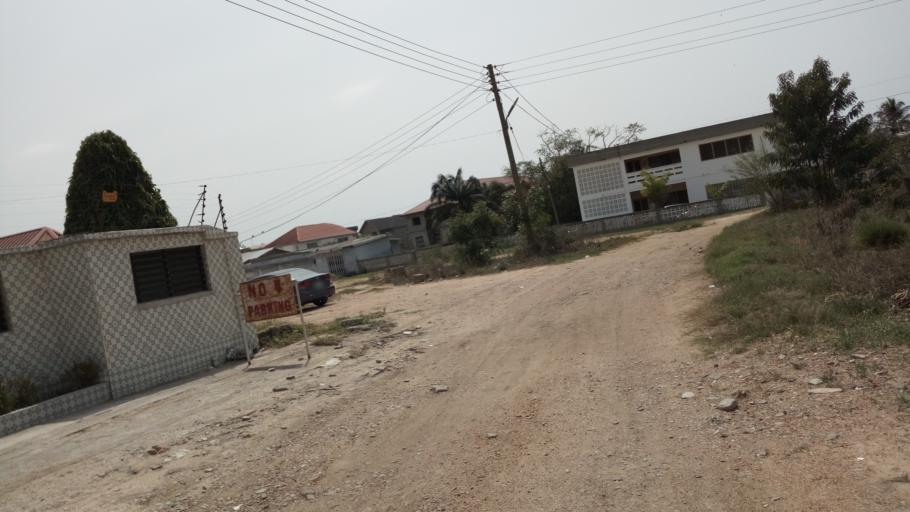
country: GH
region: Central
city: Winneba
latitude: 5.3665
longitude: -0.6427
